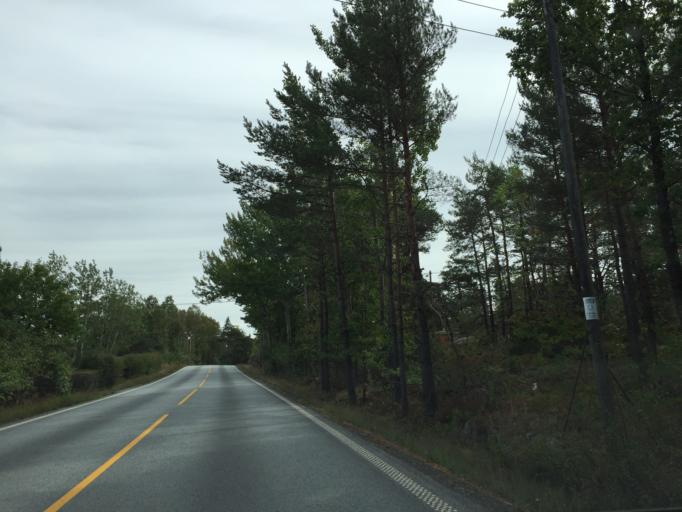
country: NO
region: Ostfold
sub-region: Hvaler
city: Skjaerhalden
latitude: 59.0661
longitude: 10.9363
